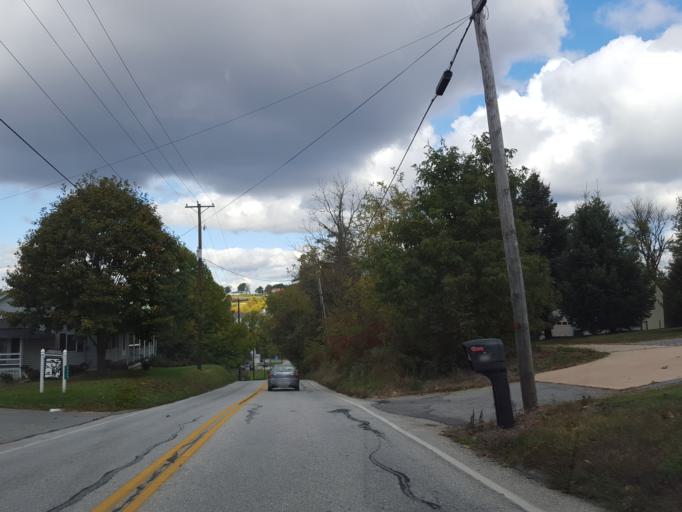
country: US
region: Pennsylvania
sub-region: York County
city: Spry
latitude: 39.9331
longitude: -76.6759
